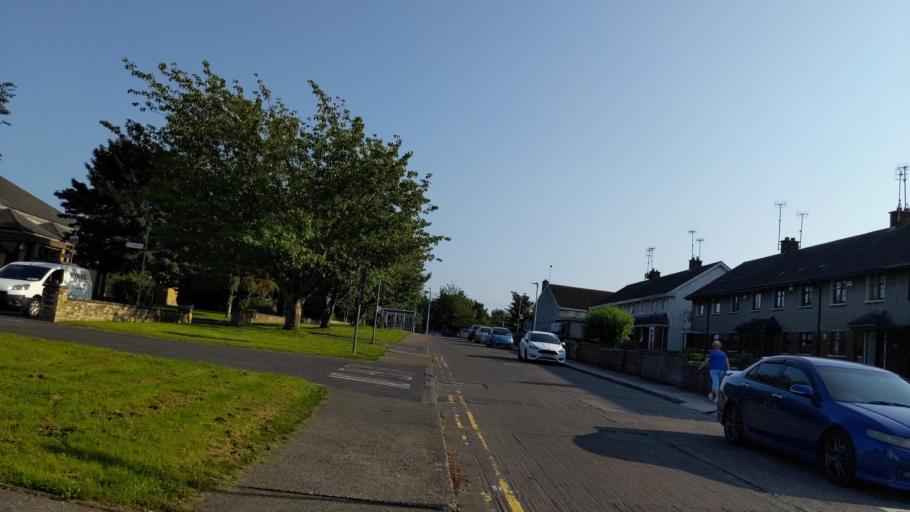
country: IE
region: Leinster
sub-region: Lu
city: Drogheda
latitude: 53.7128
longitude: -6.3606
